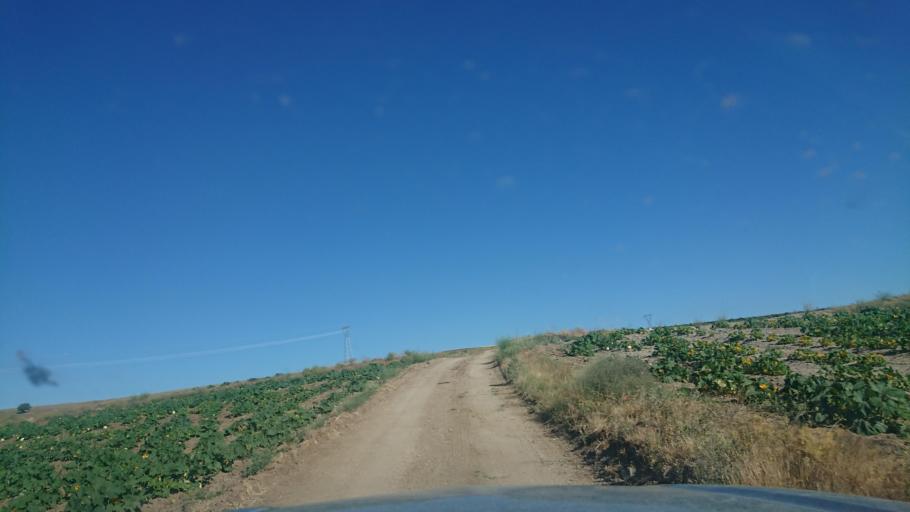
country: TR
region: Aksaray
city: Agacoren
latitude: 38.8323
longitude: 33.9498
